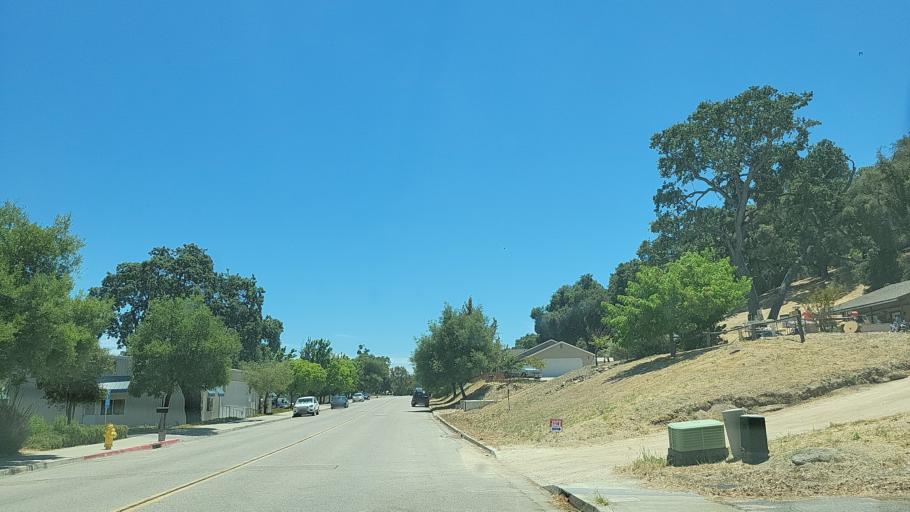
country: US
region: California
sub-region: San Luis Obispo County
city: Atascadero
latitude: 35.5107
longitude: -120.6717
